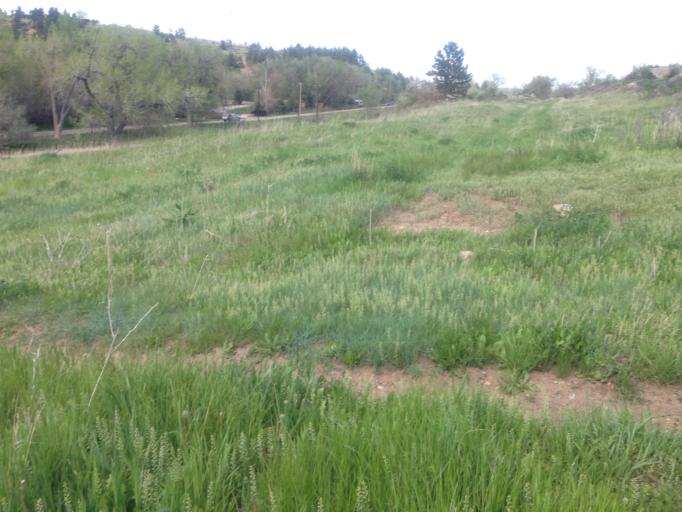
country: US
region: Colorado
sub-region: Boulder County
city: Superior
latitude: 39.9549
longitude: -105.2181
